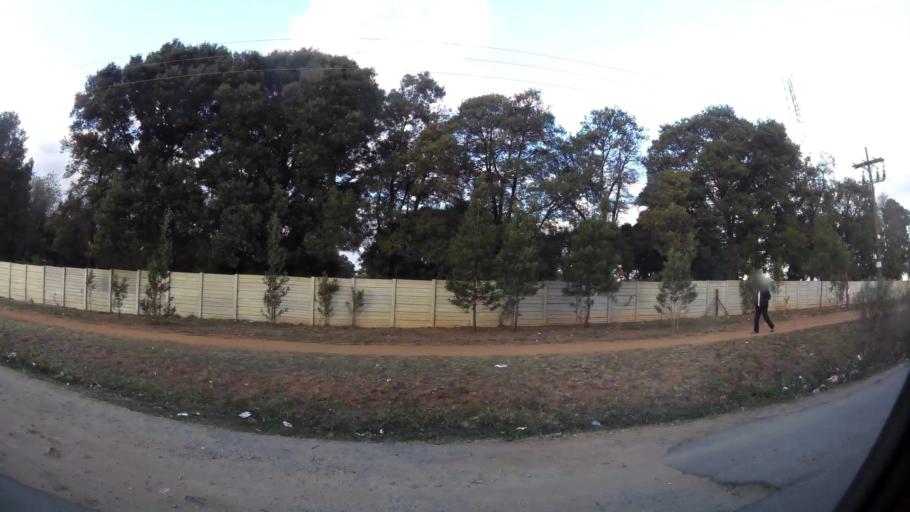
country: ZA
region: Gauteng
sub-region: City of Johannesburg Metropolitan Municipality
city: Midrand
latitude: -25.9883
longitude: 28.1529
